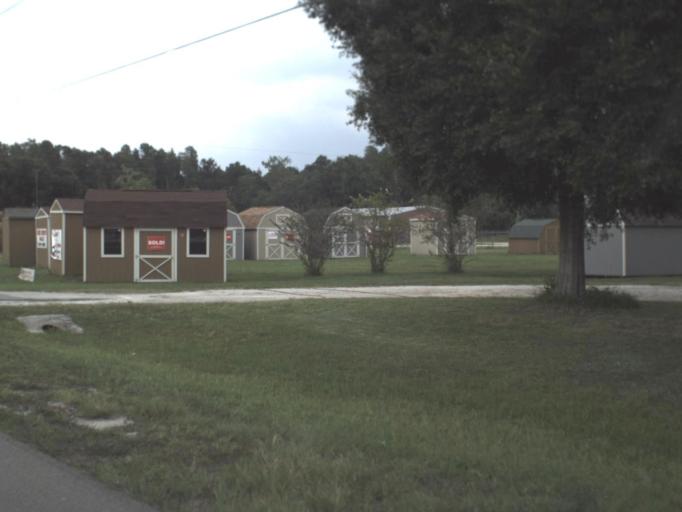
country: US
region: Florida
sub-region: Pasco County
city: Shady Hills
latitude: 28.3458
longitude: -82.5029
